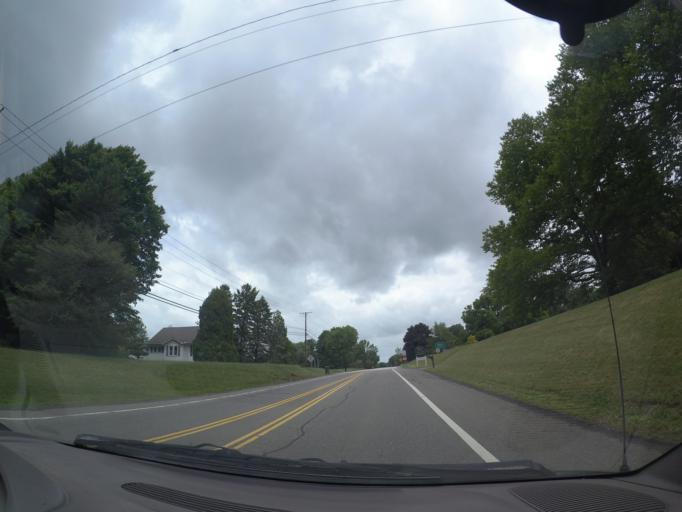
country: US
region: Ohio
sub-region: Ashtabula County
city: Geneva
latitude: 41.7830
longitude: -80.9467
